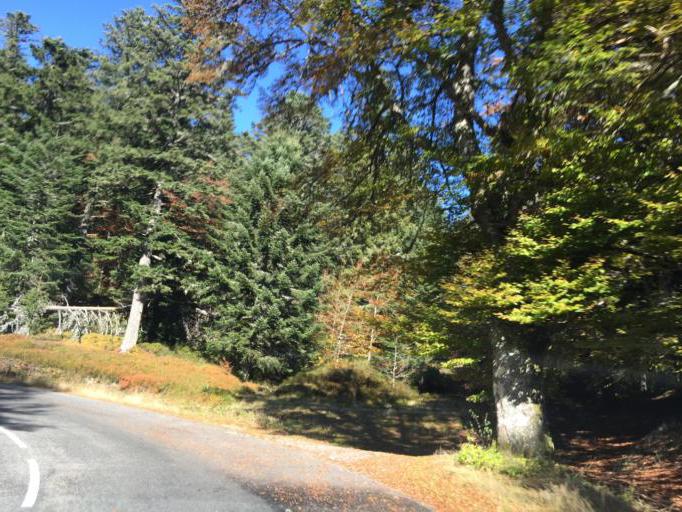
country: FR
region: Rhone-Alpes
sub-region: Departement de la Loire
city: Saint-Julien-Molin-Molette
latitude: 45.3780
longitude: 4.5650
